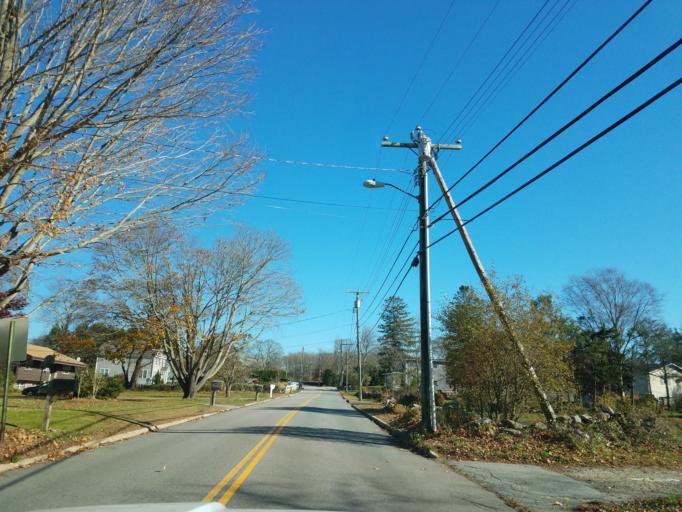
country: US
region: Connecticut
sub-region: New London County
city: Central Waterford
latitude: 41.3238
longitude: -72.1437
